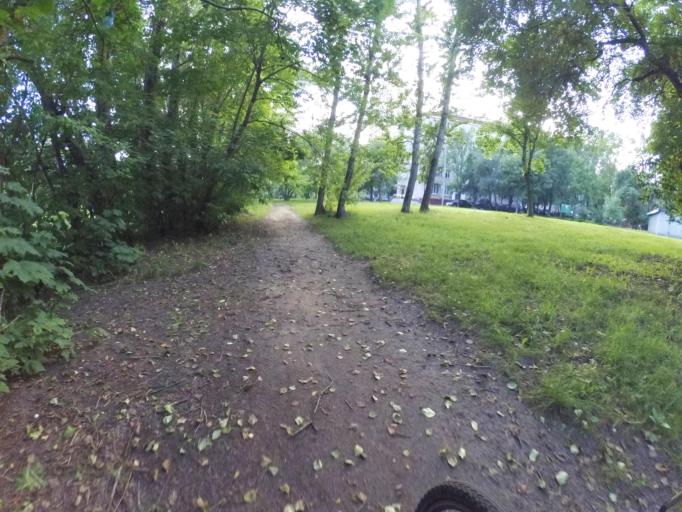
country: RU
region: Moskovskaya
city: Levoberezhnyy
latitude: 55.8369
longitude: 37.4636
